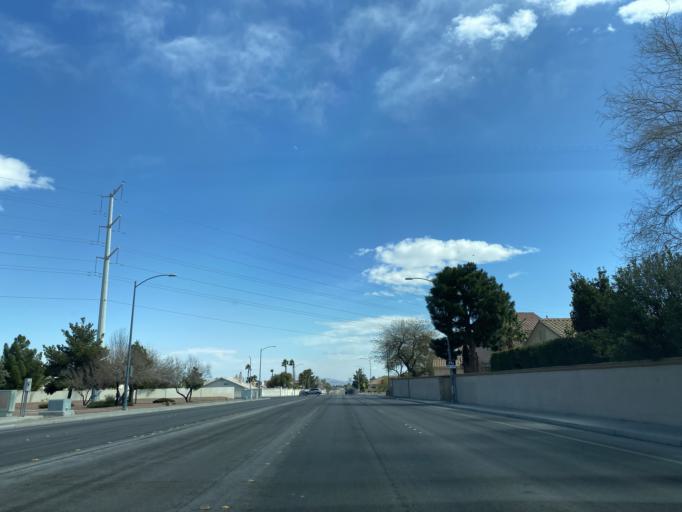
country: US
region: Nevada
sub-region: Clark County
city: Spring Valley
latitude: 36.2260
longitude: -115.2713
